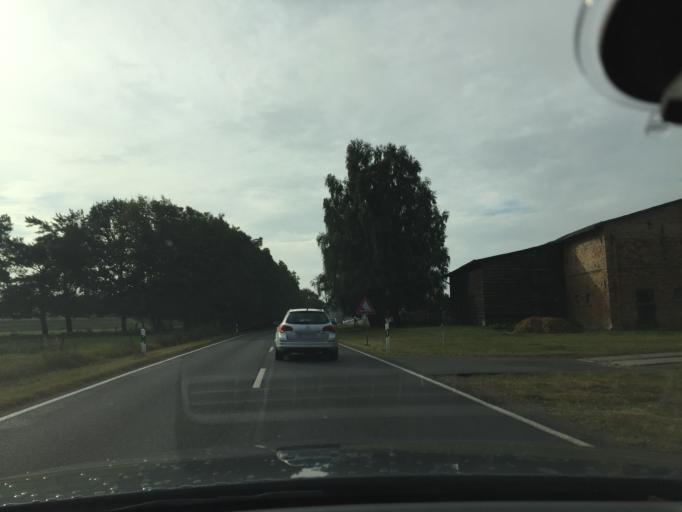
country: DE
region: Mecklenburg-Vorpommern
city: Ostseebad Dierhagen
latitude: 54.2308
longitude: 12.3650
